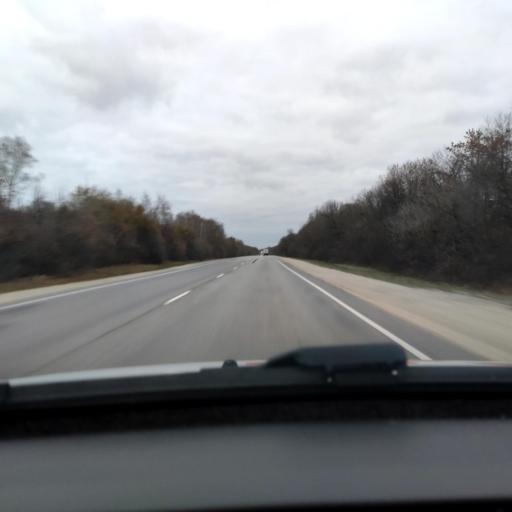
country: RU
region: Lipetsk
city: Borinskoye
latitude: 52.3776
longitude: 39.2159
